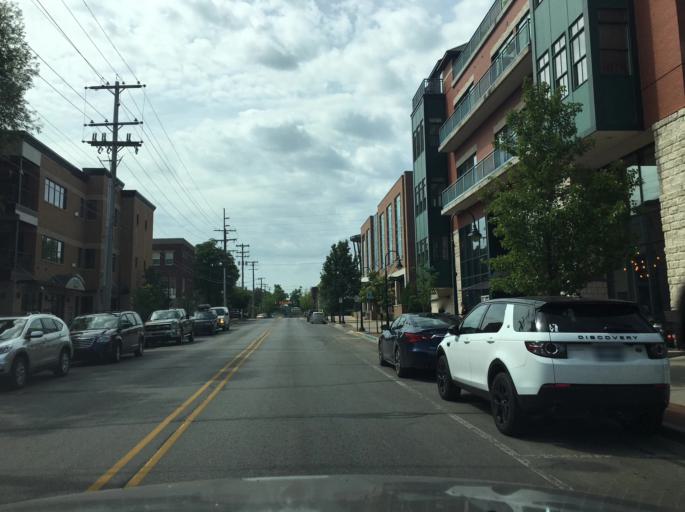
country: US
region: Michigan
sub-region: Grand Traverse County
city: Traverse City
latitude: 44.7613
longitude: -85.6210
